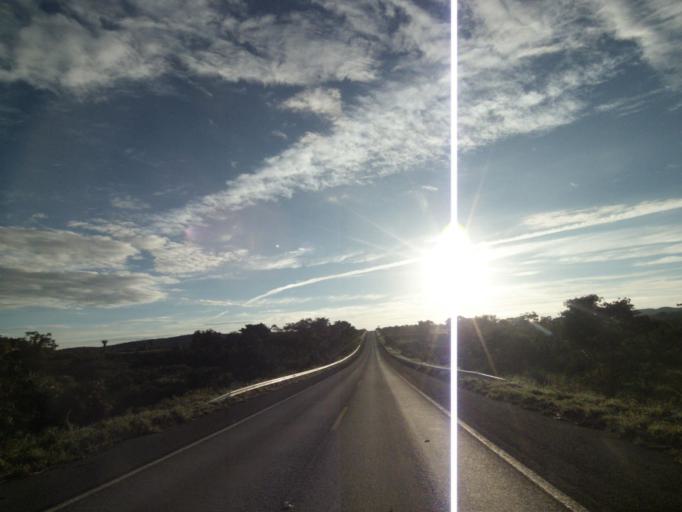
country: BR
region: Goias
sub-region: Pirenopolis
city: Pirenopolis
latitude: -15.7509
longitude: -48.6295
